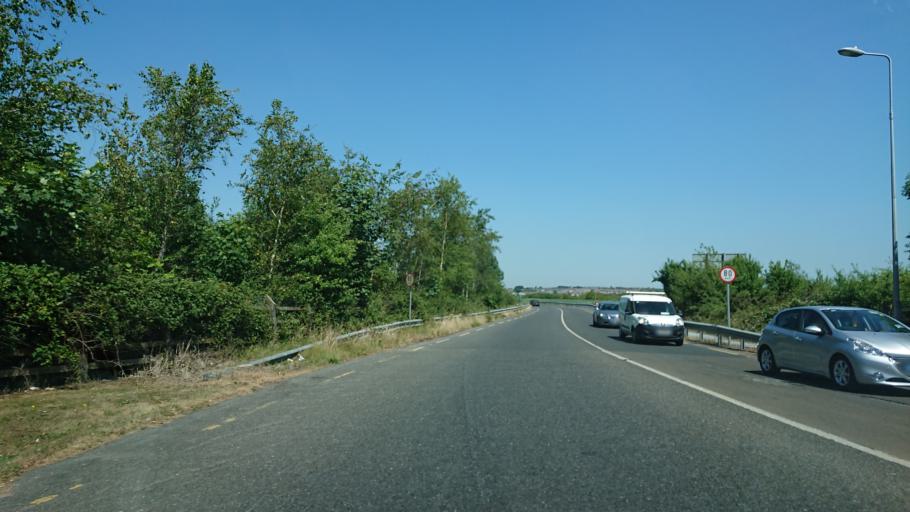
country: IE
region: Munster
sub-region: Waterford
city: Waterford
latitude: 52.2247
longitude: -7.1271
